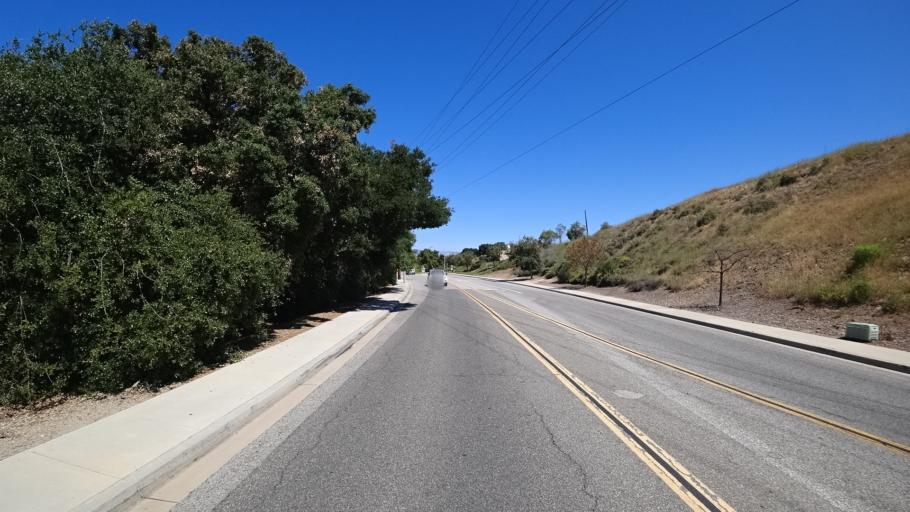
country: US
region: California
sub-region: Ventura County
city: Casa Conejo
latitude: 34.1656
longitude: -118.9562
